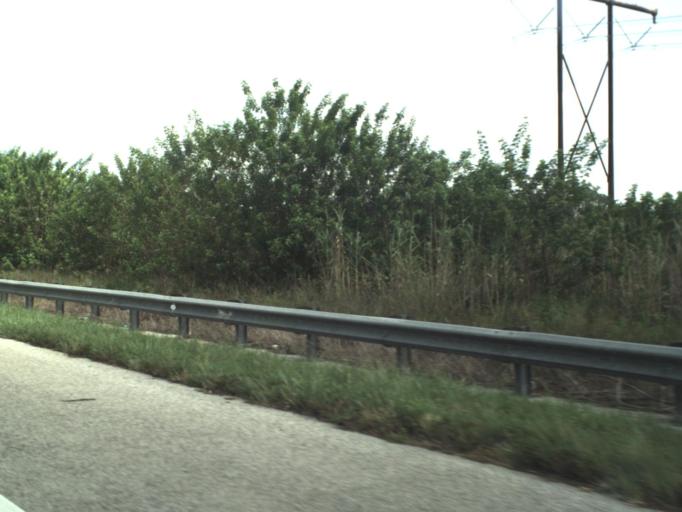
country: US
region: Florida
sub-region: Broward County
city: Weston
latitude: 26.2720
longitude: -80.4891
